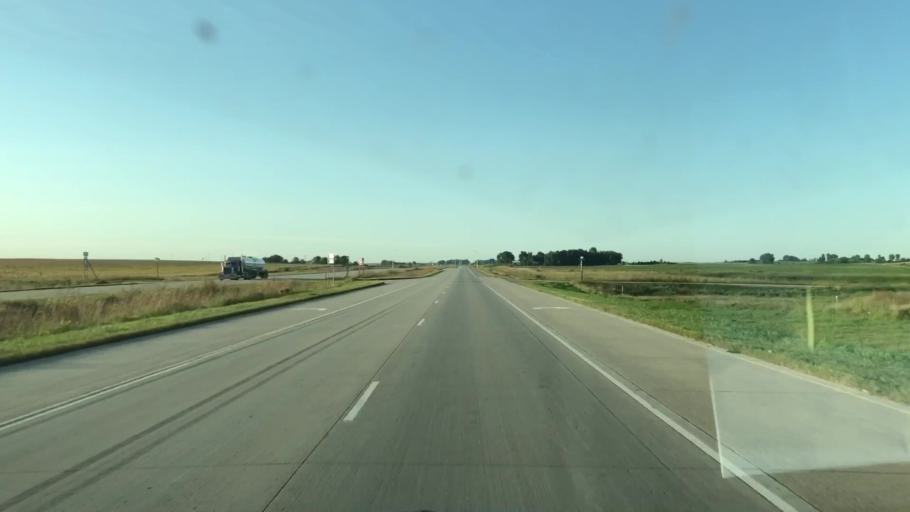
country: US
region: Minnesota
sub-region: Nobles County
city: Worthington
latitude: 43.5735
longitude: -95.6536
